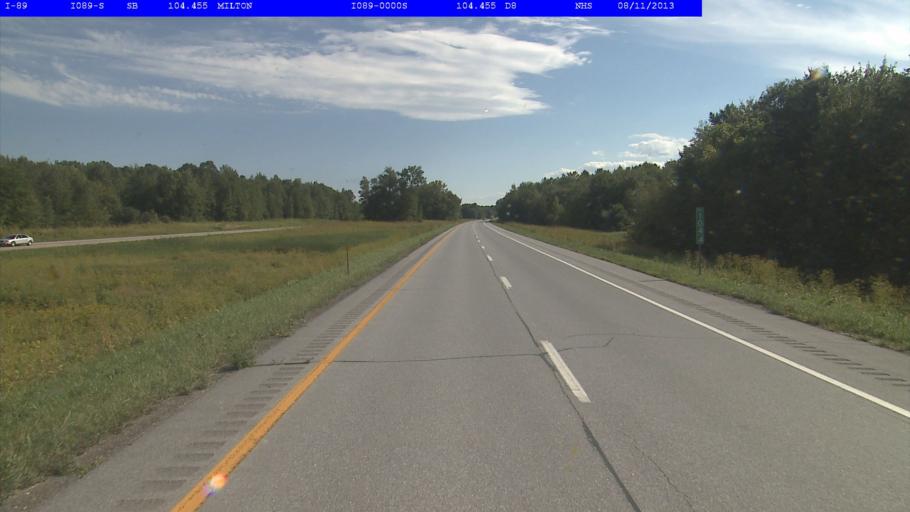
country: US
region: Vermont
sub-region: Chittenden County
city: Milton
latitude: 44.6767
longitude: -73.1309
